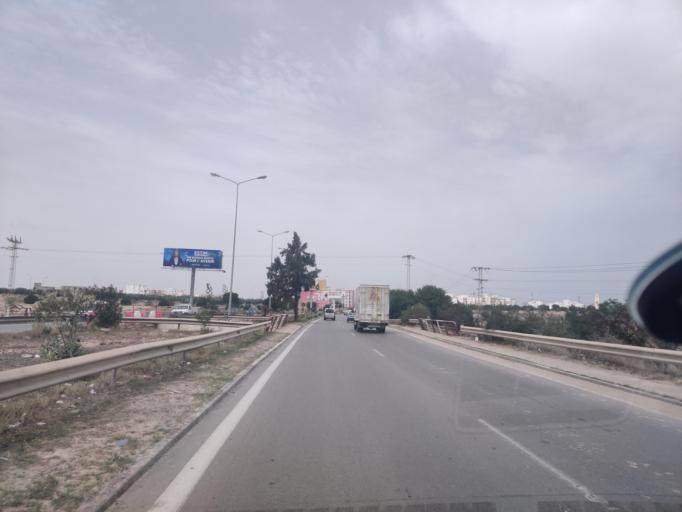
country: TN
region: Susah
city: Hammam Sousse
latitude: 35.8252
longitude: 10.5919
